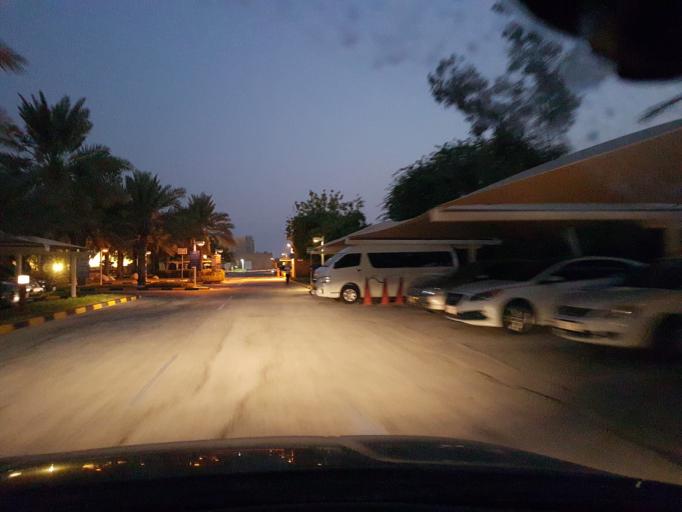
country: BH
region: Central Governorate
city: Dar Kulayb
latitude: 26.0151
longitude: 50.5086
